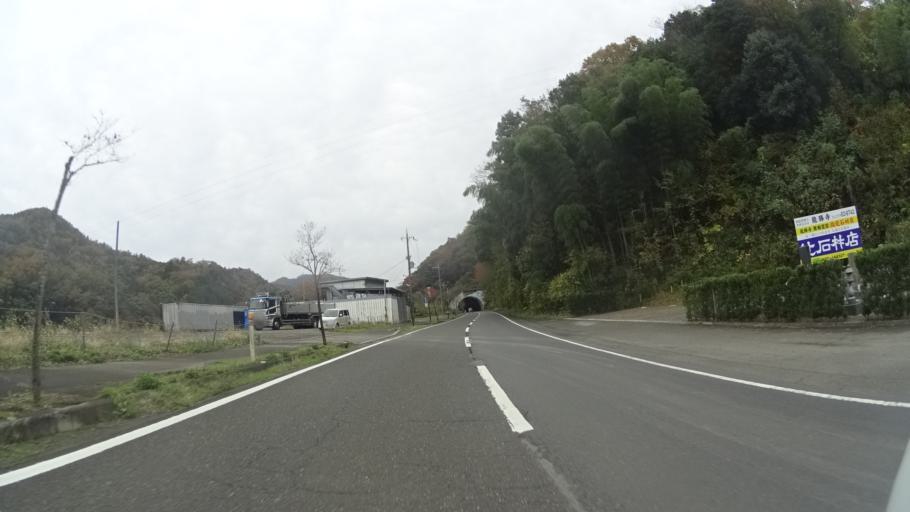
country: JP
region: Kyoto
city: Maizuru
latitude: 35.4637
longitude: 135.4130
